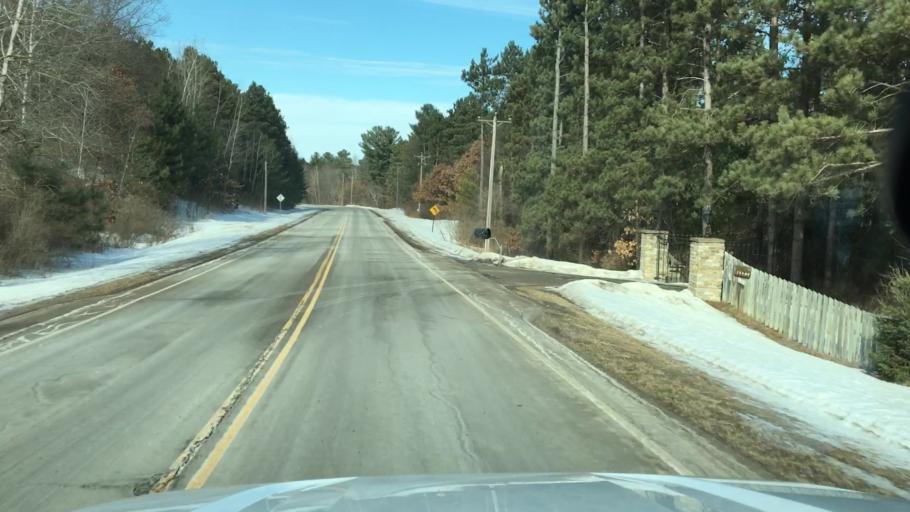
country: US
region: Wisconsin
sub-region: Polk County
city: Saint Croix Falls
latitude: 45.4566
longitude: -92.6733
